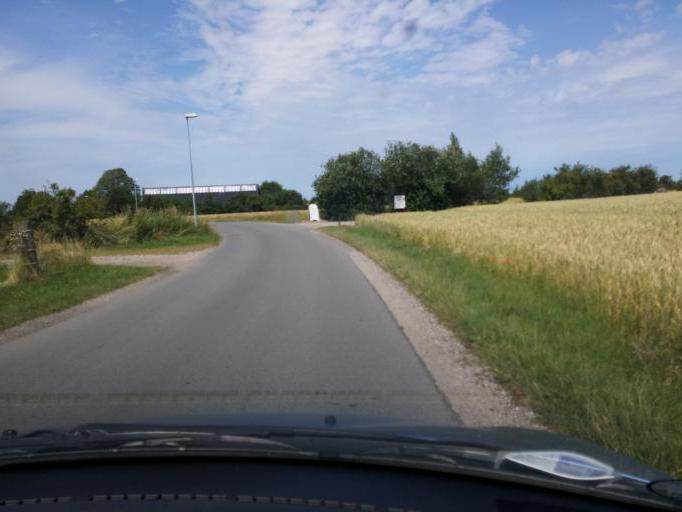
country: DK
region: South Denmark
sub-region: Kerteminde Kommune
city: Langeskov
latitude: 55.4087
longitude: 10.5990
